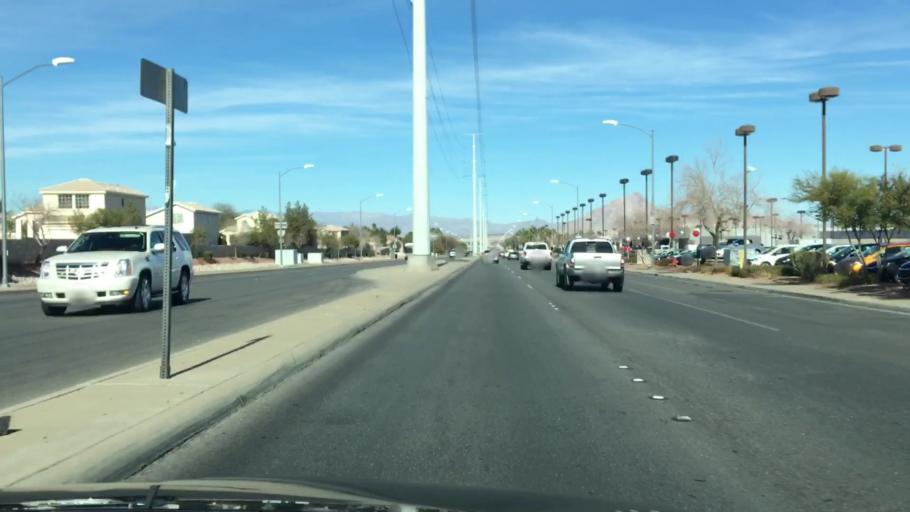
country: US
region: Nevada
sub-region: Clark County
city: Henderson
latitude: 36.0462
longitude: -115.0287
